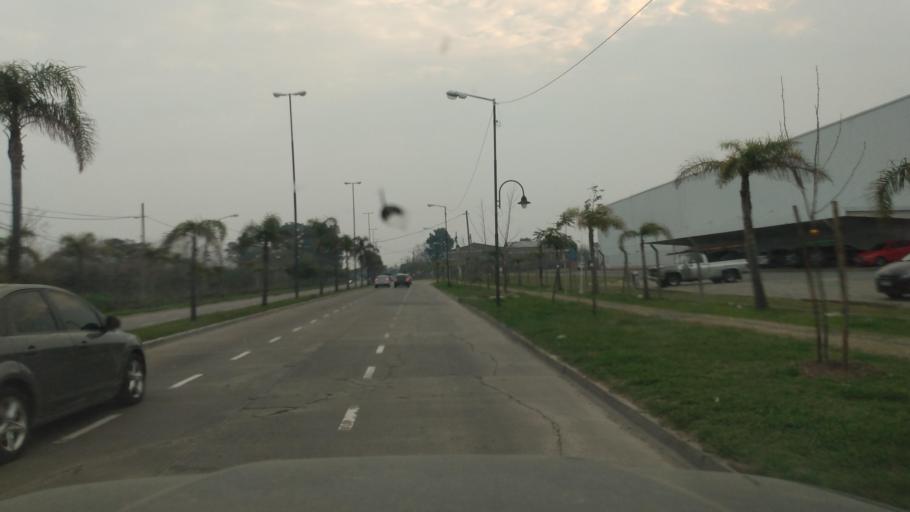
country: AR
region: Buenos Aires
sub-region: Partido de Tigre
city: Tigre
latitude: -34.4595
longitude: -58.5908
